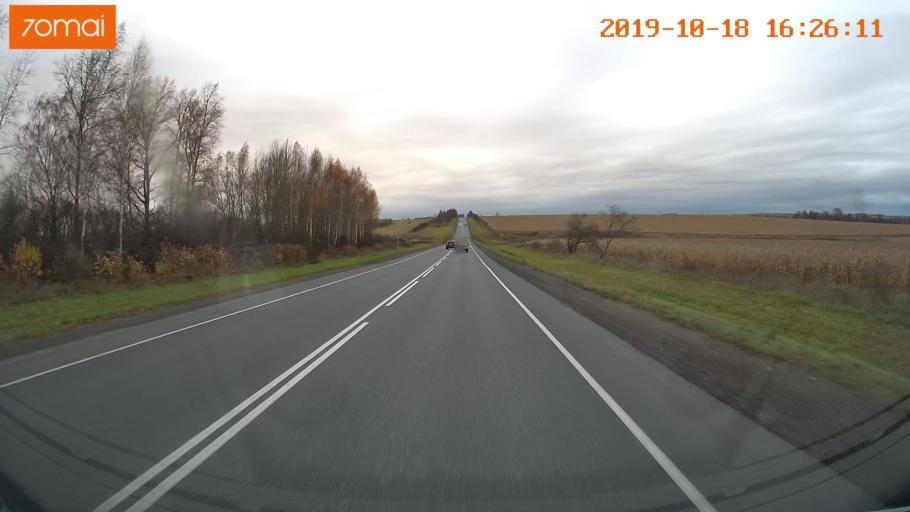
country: RU
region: Vladimir
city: Bogolyubovo
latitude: 56.2851
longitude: 40.4674
